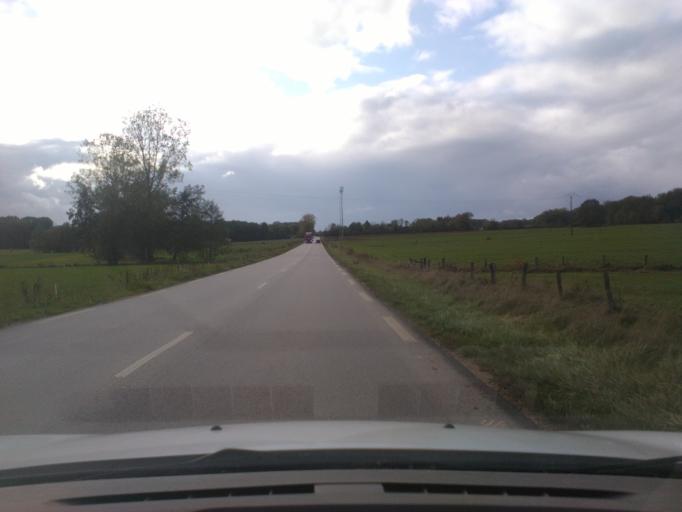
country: FR
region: Lorraine
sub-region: Departement des Vosges
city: Aydoilles
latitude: 48.2477
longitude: 6.6175
